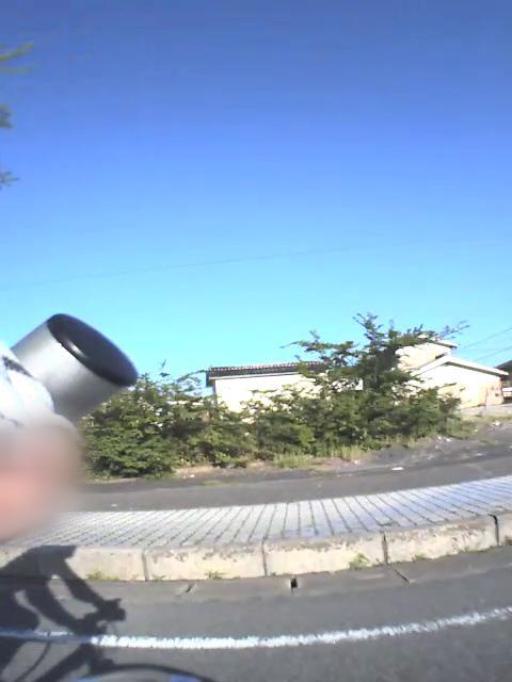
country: JP
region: Yamaguchi
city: Nagato
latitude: 34.3941
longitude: 131.2001
